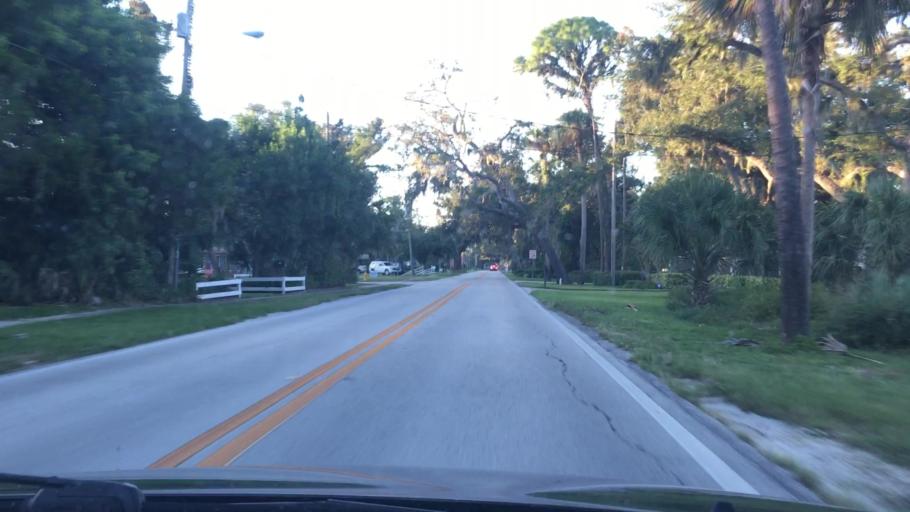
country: US
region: Florida
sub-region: Volusia County
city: Ormond Beach
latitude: 29.2967
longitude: -81.0607
